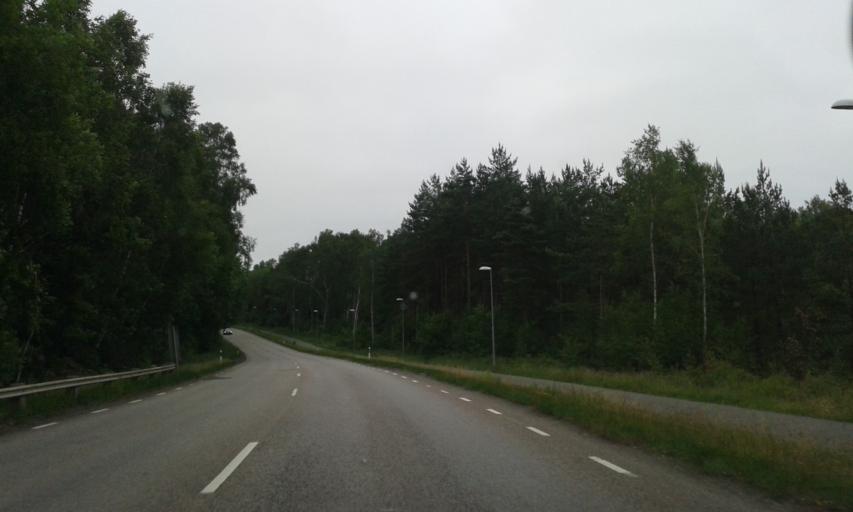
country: SE
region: Vaestra Goetaland
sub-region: Partille Kommun
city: Partille
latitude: 57.7533
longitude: 12.0787
